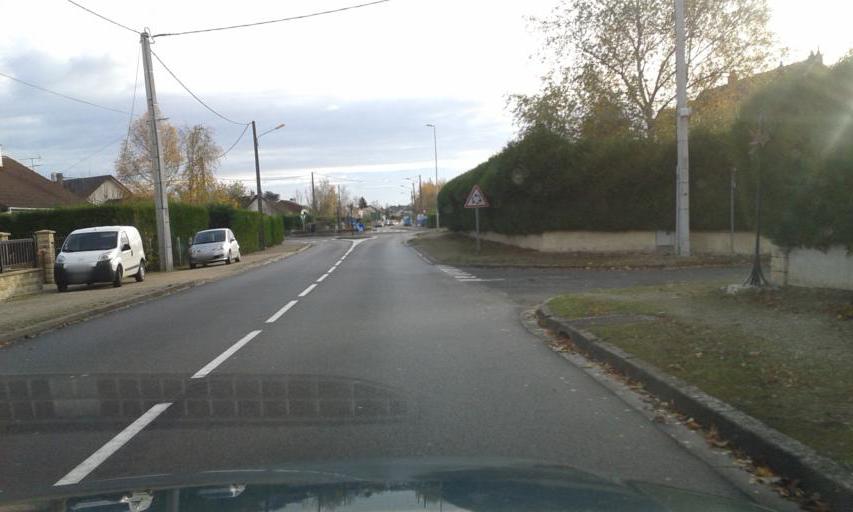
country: FR
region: Centre
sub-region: Departement du Loiret
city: Beaugency
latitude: 47.7903
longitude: 1.6280
